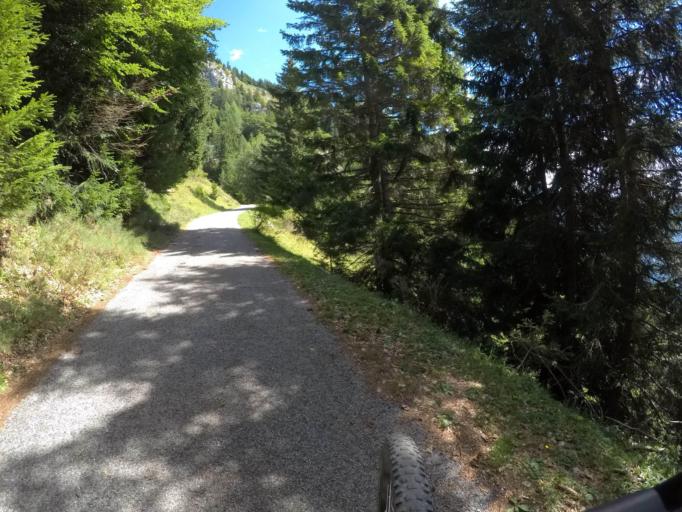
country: IT
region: Friuli Venezia Giulia
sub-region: Provincia di Udine
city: Ligosullo
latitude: 46.4994
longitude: 13.0676
